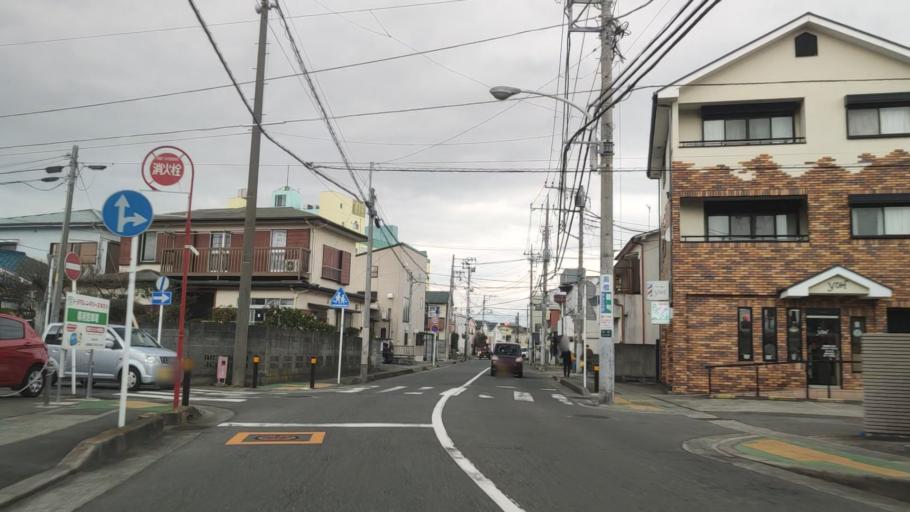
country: JP
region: Kanagawa
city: Odawara
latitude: 35.2560
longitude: 139.1636
